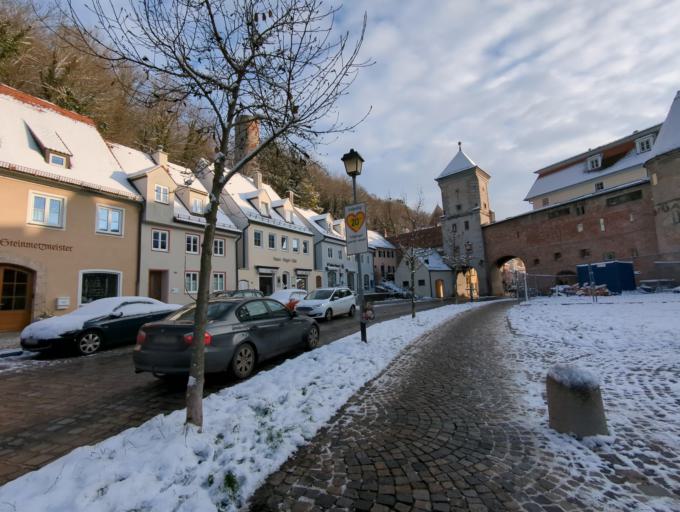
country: DE
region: Bavaria
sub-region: Upper Bavaria
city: Landsberg am Lech
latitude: 48.0538
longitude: 10.8774
